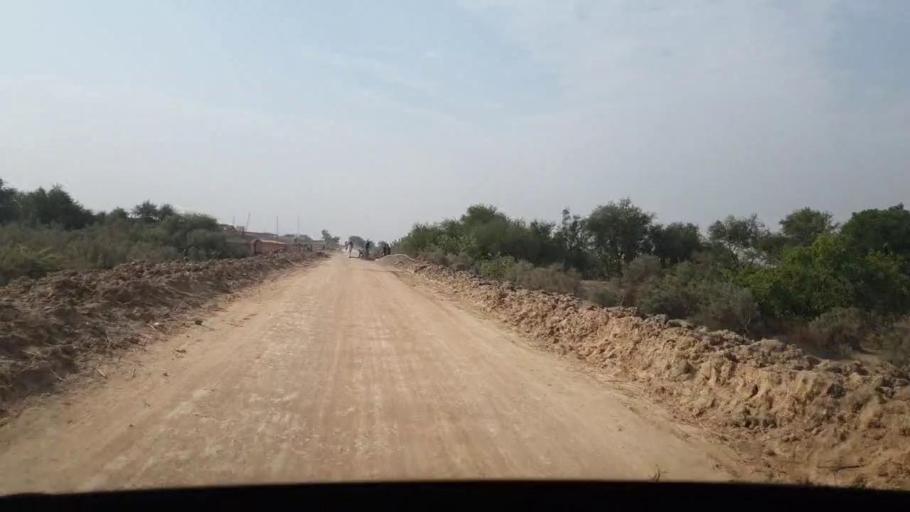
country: PK
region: Sindh
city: Chuhar Jamali
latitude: 24.3666
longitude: 67.9406
